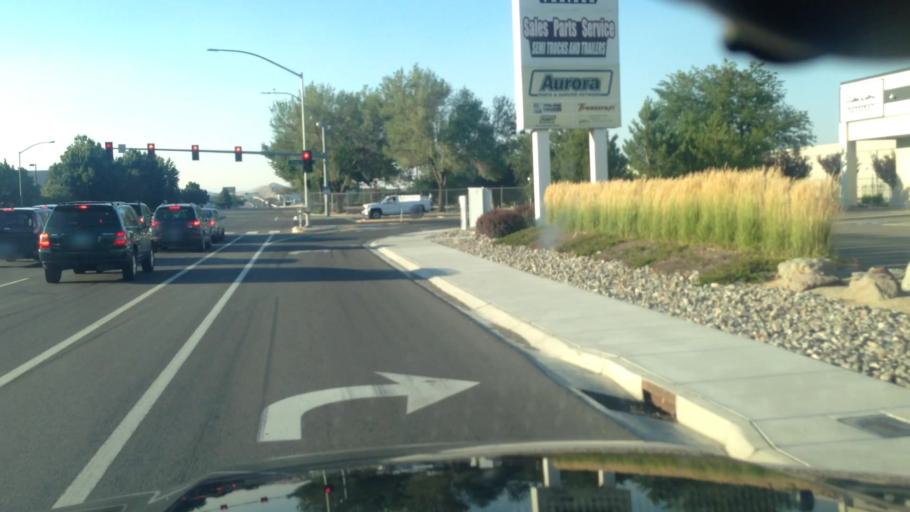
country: US
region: Nevada
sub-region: Washoe County
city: Sparks
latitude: 39.5208
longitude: -119.7401
